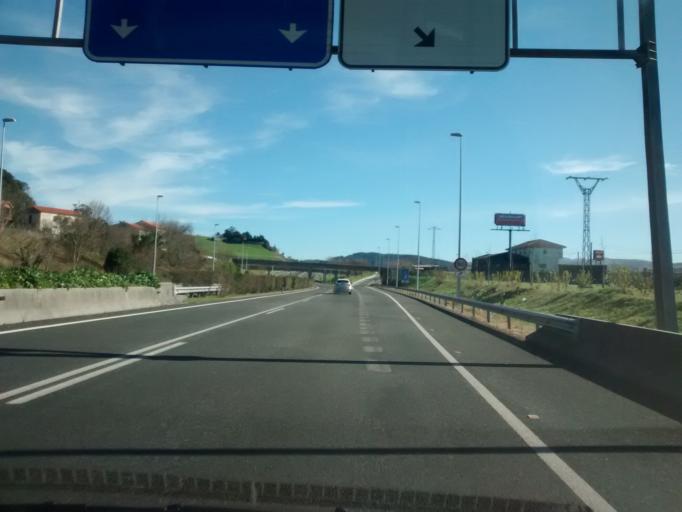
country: ES
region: Cantabria
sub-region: Provincia de Cantabria
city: Entrambasaguas
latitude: 43.3899
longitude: -3.6882
